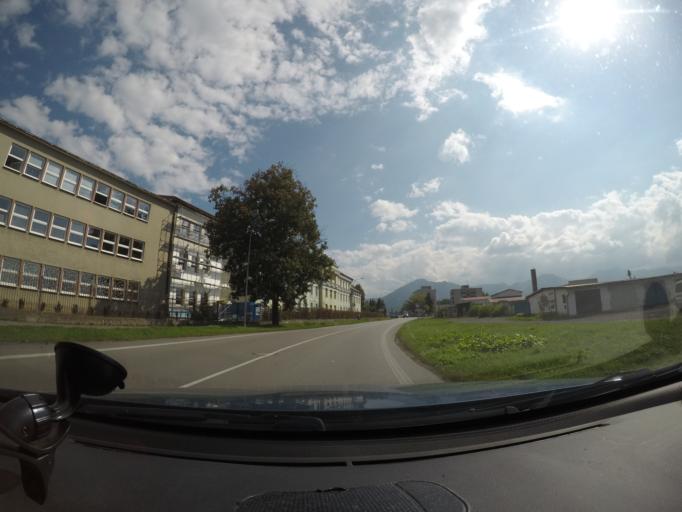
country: SK
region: Zilinsky
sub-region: Okres Liptovsky Mikulas
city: Liptovsky Mikulas
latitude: 49.0893
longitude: 19.6027
